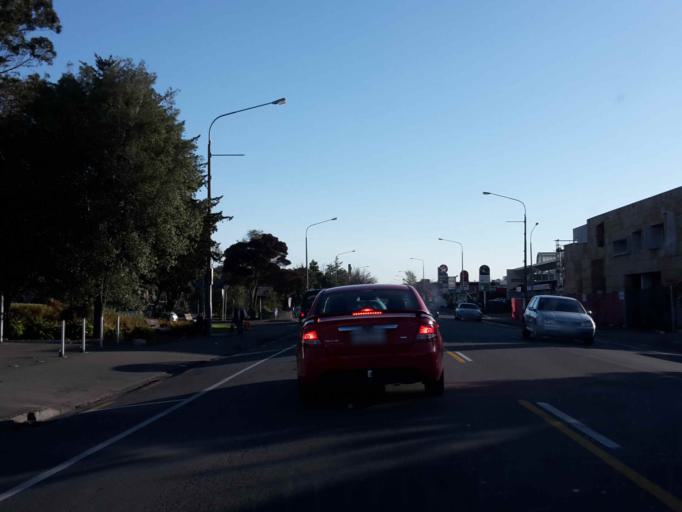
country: NZ
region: Canterbury
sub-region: Christchurch City
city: Christchurch
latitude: -43.5292
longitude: 172.6069
